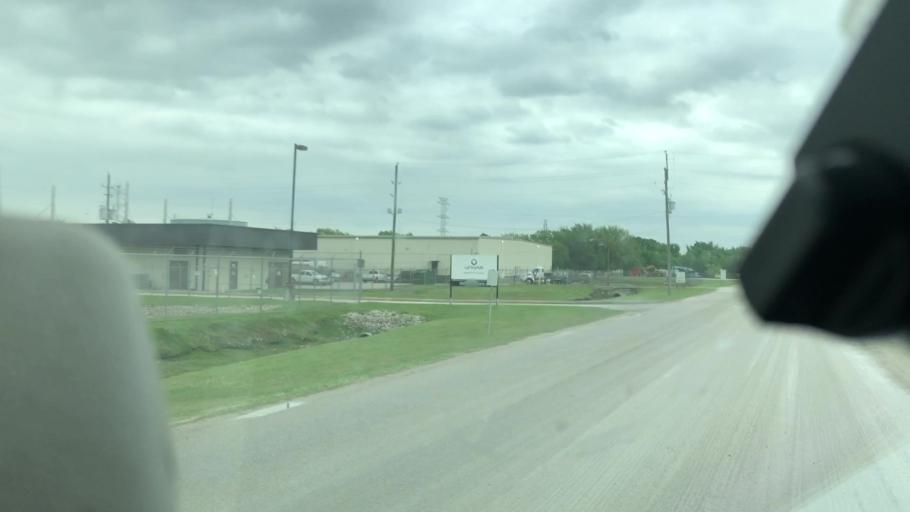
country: US
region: Texas
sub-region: Harris County
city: Jersey Village
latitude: 29.8756
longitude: -95.5799
